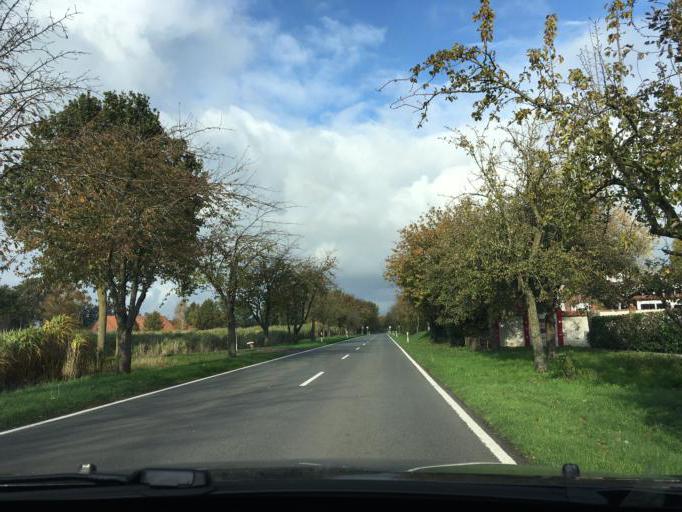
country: DE
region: North Rhine-Westphalia
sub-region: Regierungsbezirk Munster
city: Vreden
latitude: 52.0631
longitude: 6.7647
